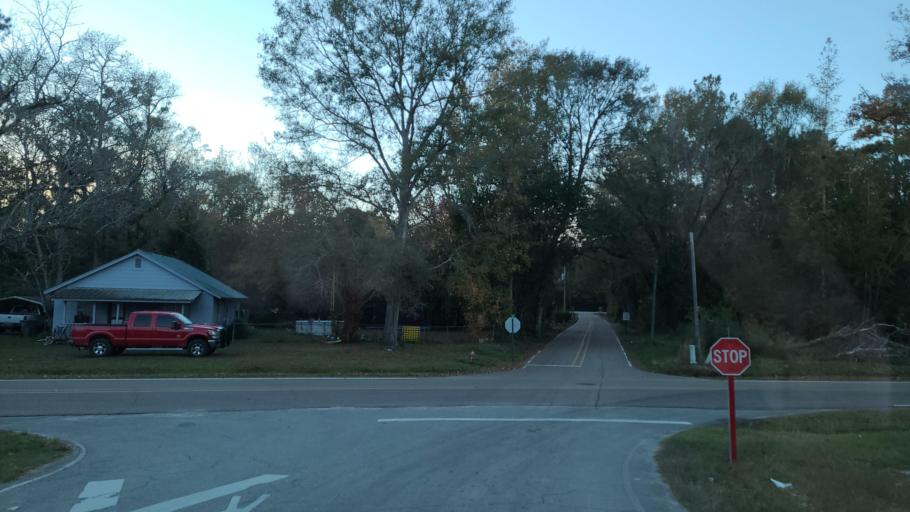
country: US
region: Mississippi
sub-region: Stone County
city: Wiggins
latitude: 31.0590
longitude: -89.1881
